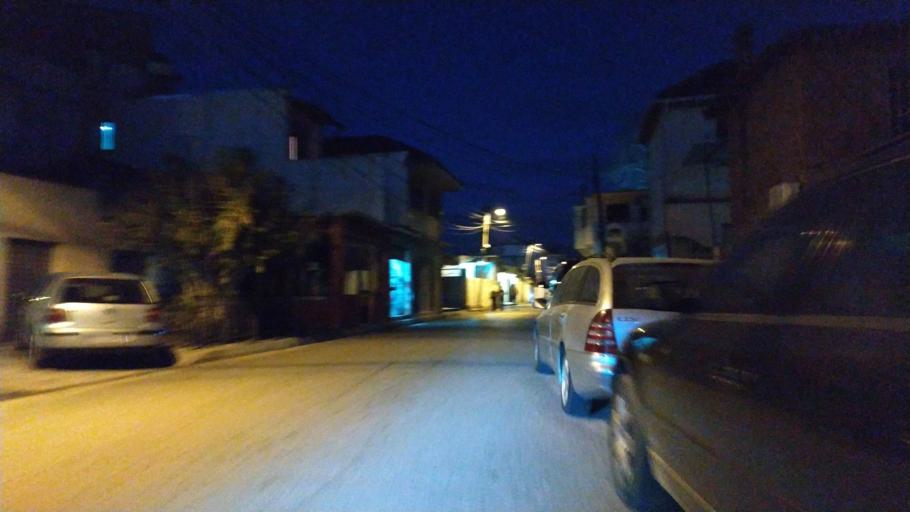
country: AL
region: Shkoder
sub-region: Rrethi i Shkodres
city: Shkoder
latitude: 42.0615
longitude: 19.5027
